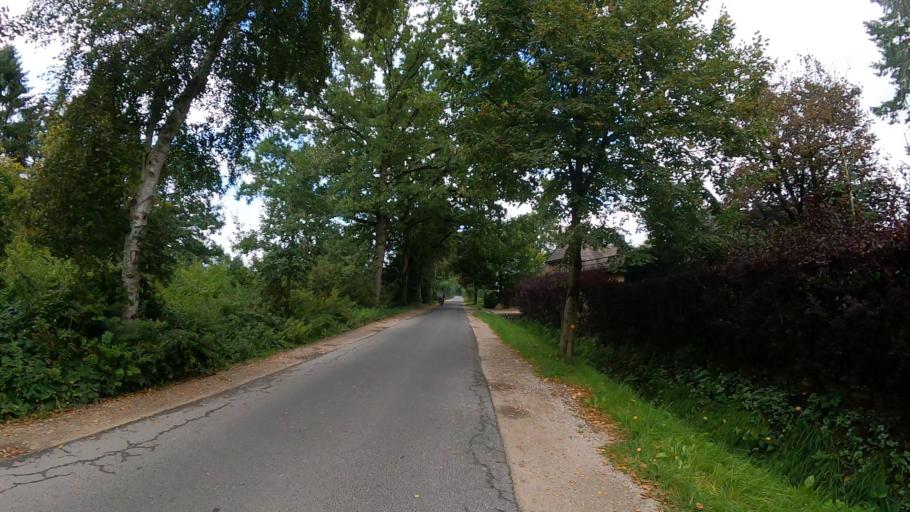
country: DE
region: Schleswig-Holstein
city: Tornesch
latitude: 53.7119
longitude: 9.7118
